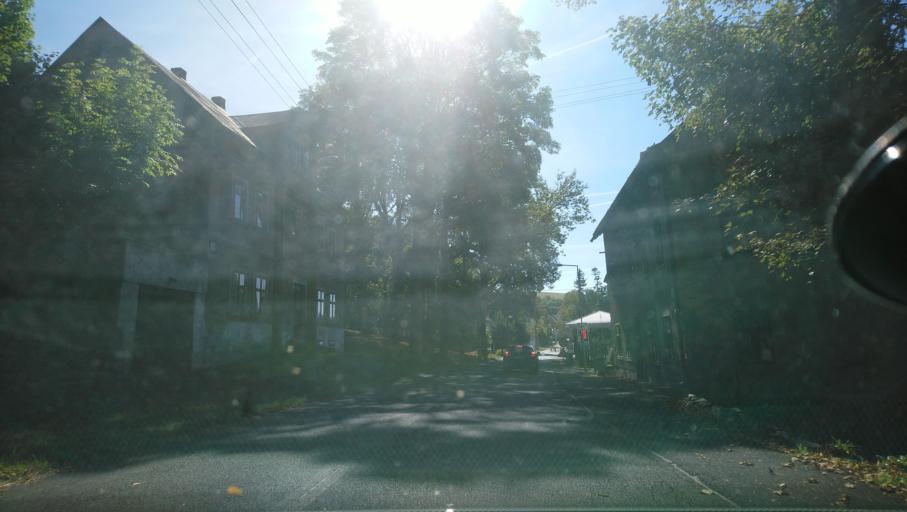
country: CZ
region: Ustecky
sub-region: Okres Chomutov
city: Vejprty
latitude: 50.4859
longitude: 13.0250
